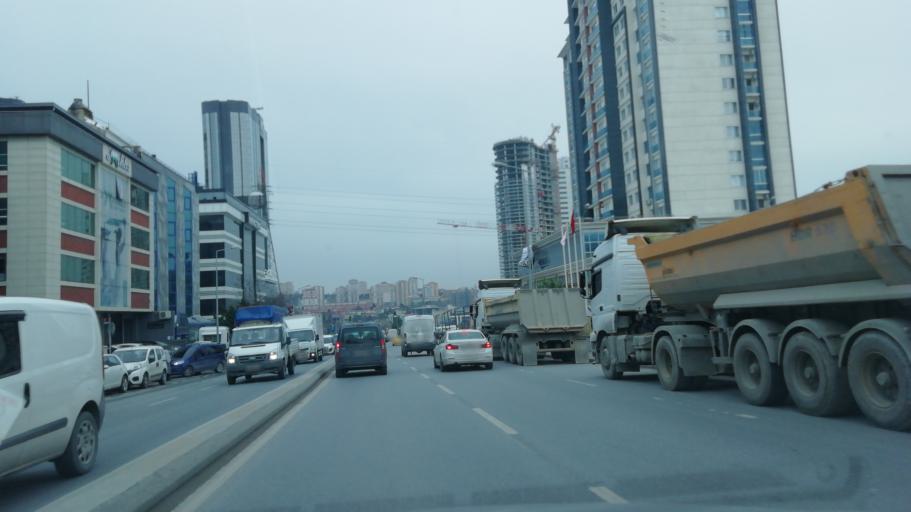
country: TR
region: Istanbul
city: Mahmutbey
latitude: 41.0452
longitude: 28.8156
